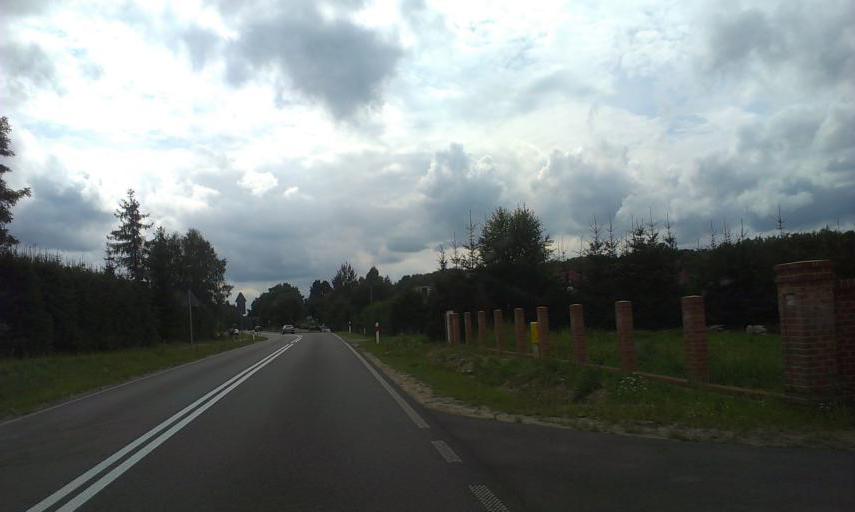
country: PL
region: West Pomeranian Voivodeship
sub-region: Koszalin
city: Koszalin
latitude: 54.1079
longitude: 16.1704
